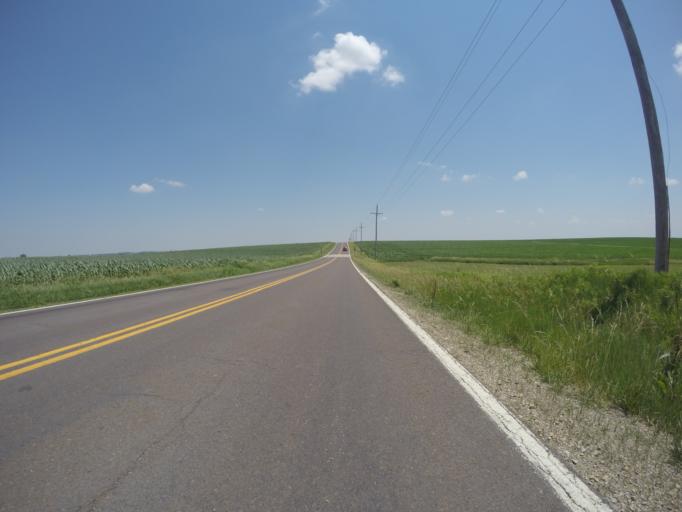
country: US
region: Kansas
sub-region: Doniphan County
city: Troy
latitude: 39.7400
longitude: -95.1509
